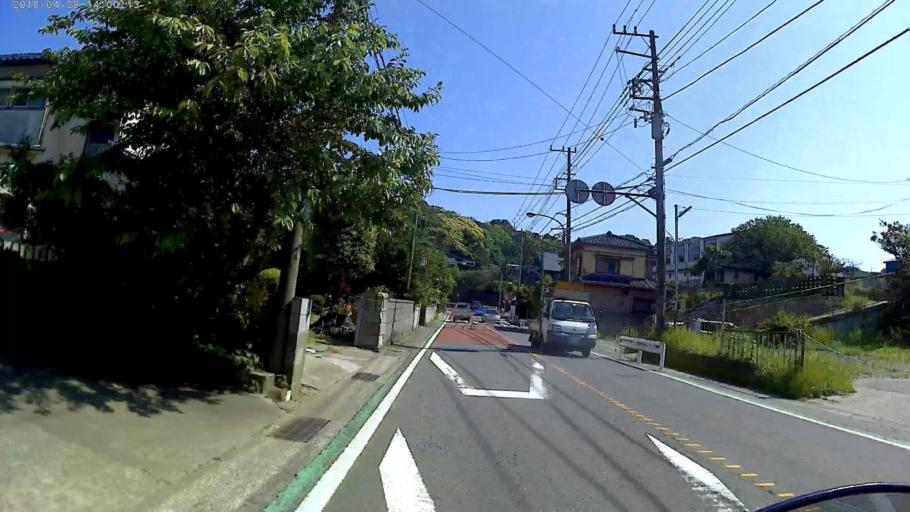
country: JP
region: Kanagawa
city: Miura
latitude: 35.1738
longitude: 139.6547
